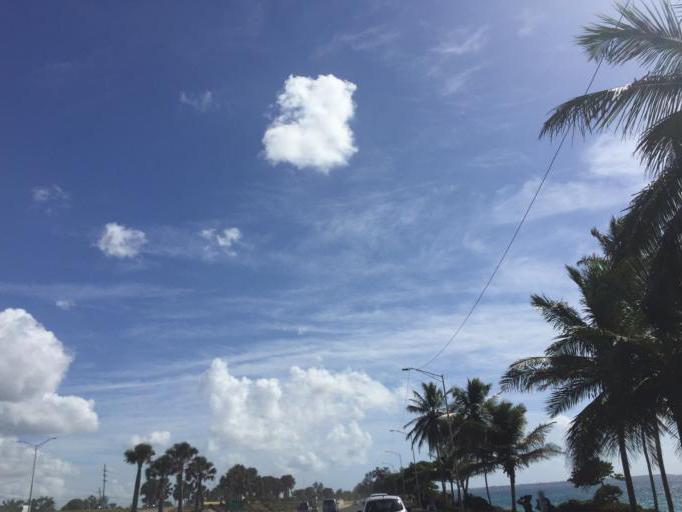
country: DO
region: Santo Domingo
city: Guerra
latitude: 18.4591
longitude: -69.7250
